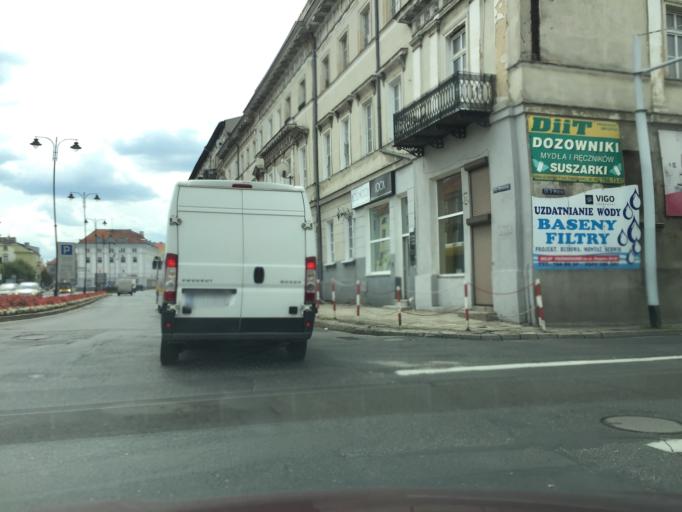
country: PL
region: Greater Poland Voivodeship
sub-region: Kalisz
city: Kalisz
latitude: 51.7661
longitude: 18.0940
